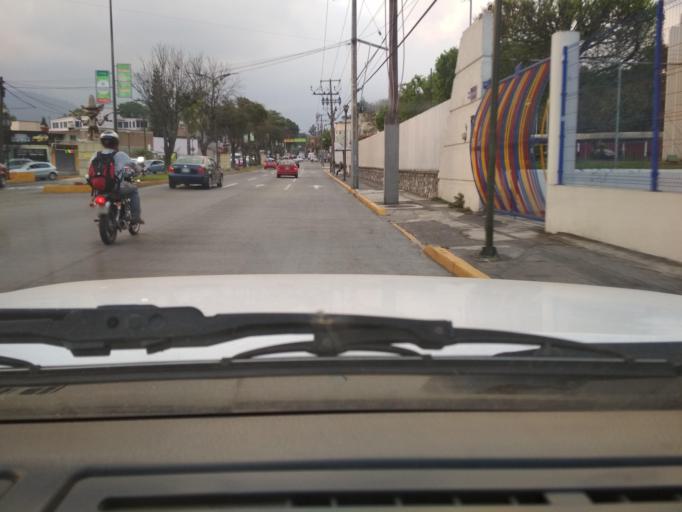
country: MX
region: Veracruz
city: Orizaba
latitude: 18.8594
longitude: -97.0926
